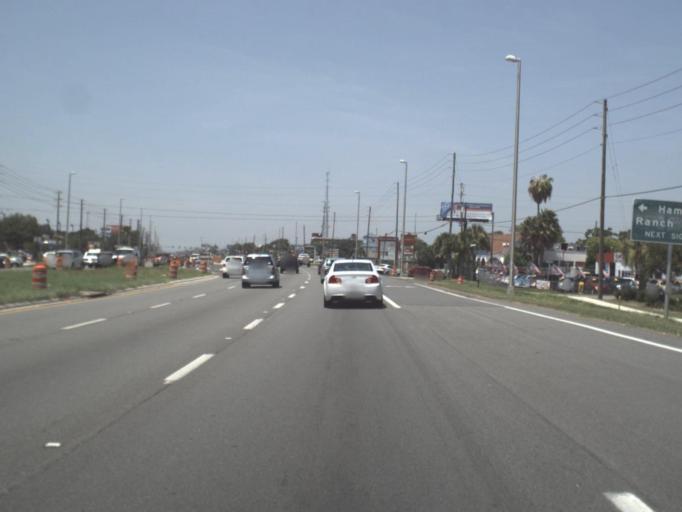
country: US
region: Florida
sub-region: Pasco County
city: Jasmine Estates
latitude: 28.3111
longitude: -82.6995
